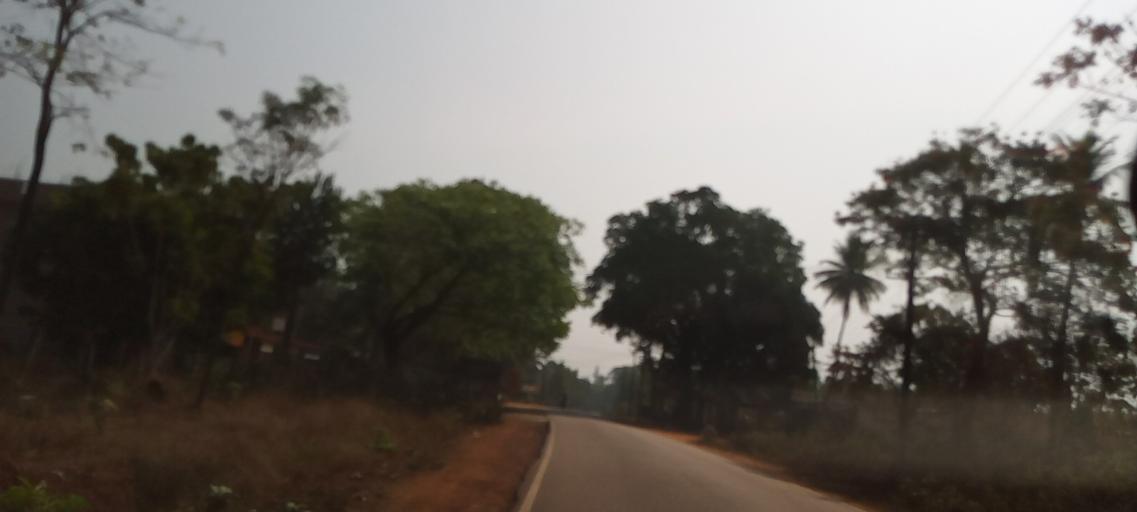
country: IN
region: Karnataka
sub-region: Udupi
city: Manipala
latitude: 13.5113
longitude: 74.8217
